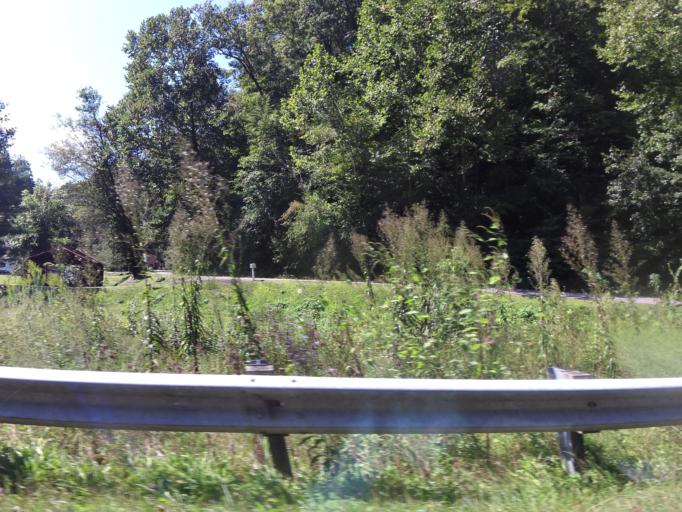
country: US
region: Kentucky
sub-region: Leslie County
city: Hyden
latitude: 37.1562
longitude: -83.5059
